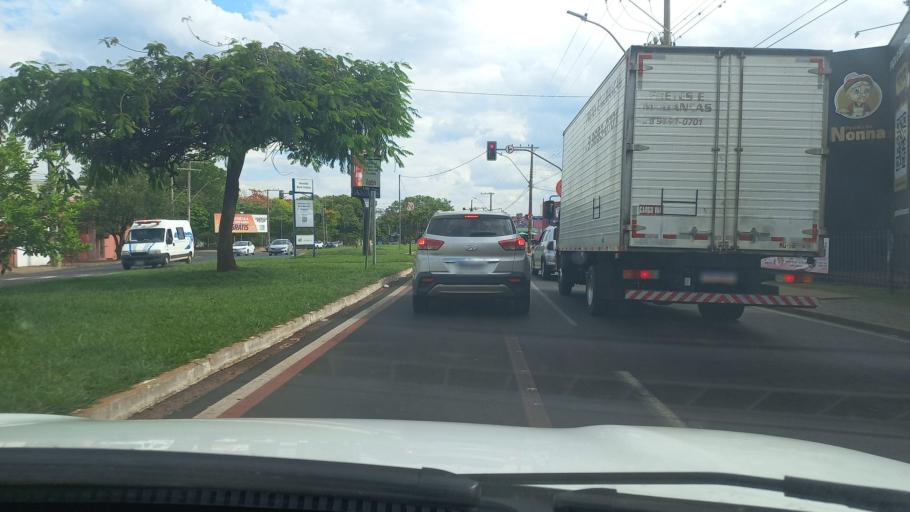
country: BR
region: Minas Gerais
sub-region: Uberaba
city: Uberaba
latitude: -19.7537
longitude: -47.9645
